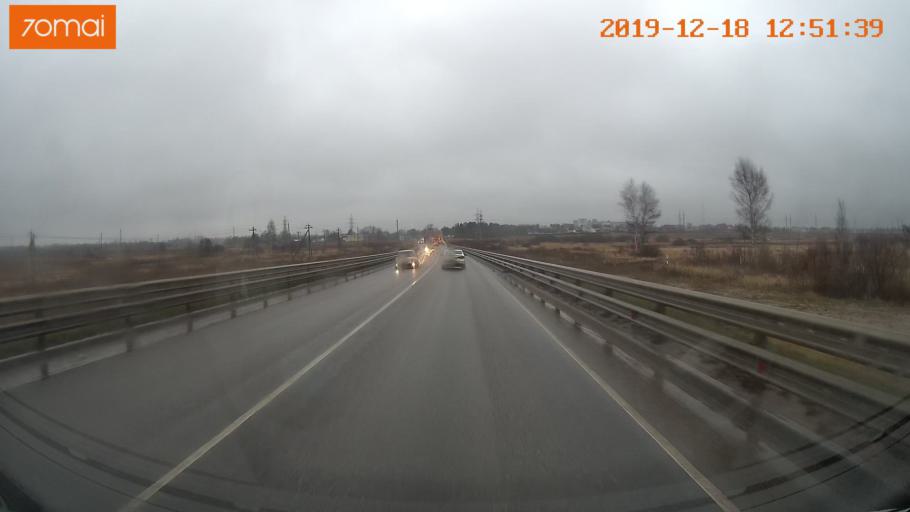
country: RU
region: Moskovskaya
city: Klin
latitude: 56.3052
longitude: 36.6847
